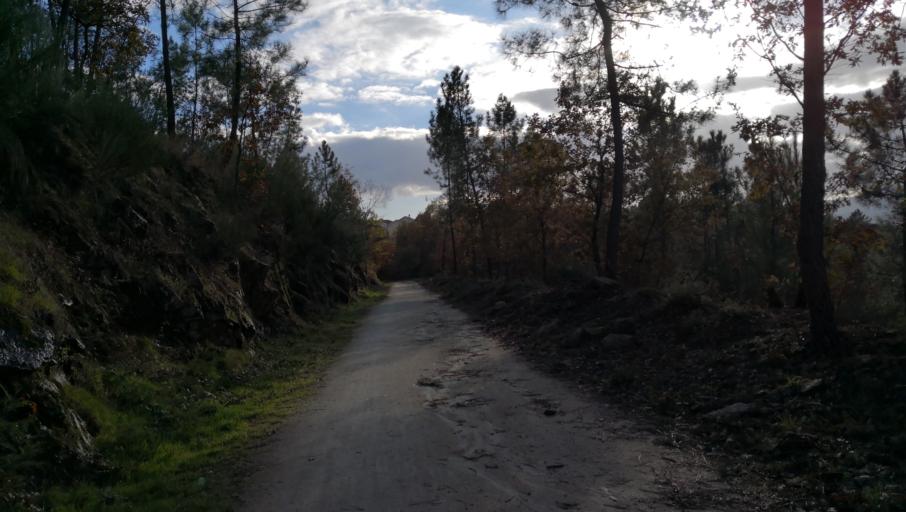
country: PT
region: Vila Real
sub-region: Vila Real
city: Vila Real
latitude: 41.3227
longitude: -7.7113
